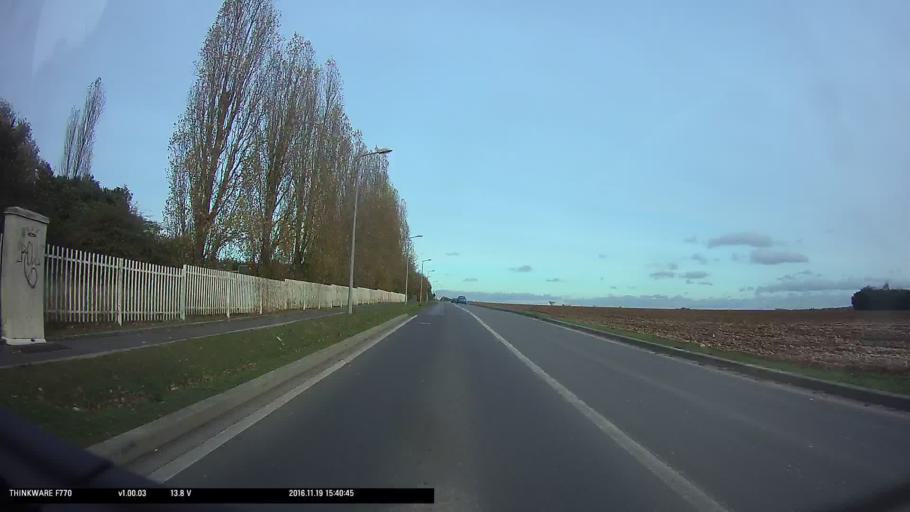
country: FR
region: Ile-de-France
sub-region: Departement du Val-d'Oise
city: Osny
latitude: 49.0815
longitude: 2.0365
